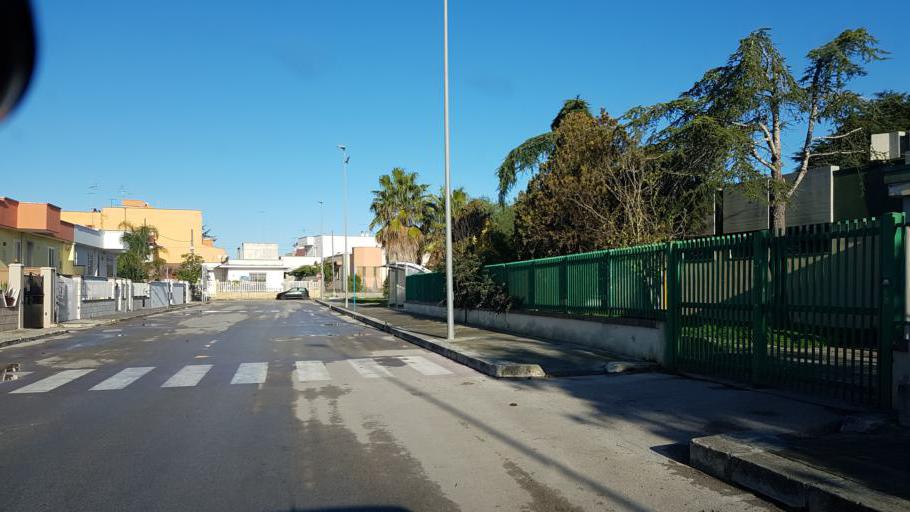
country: IT
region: Apulia
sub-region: Provincia di Brindisi
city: Torchiarolo
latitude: 40.4803
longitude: 18.0553
